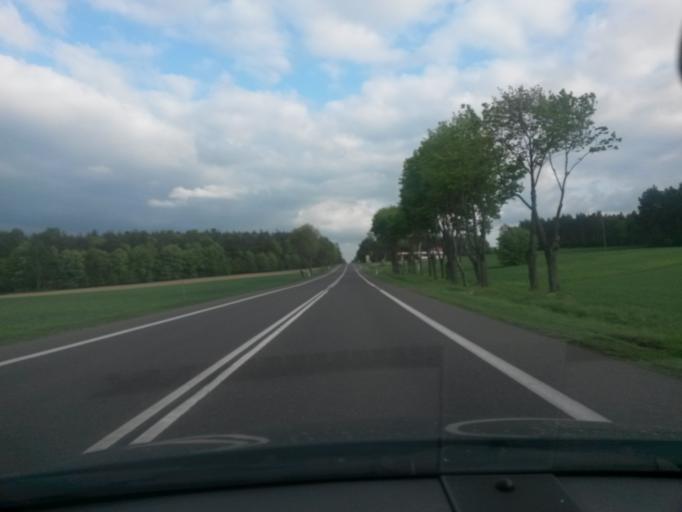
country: PL
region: Masovian Voivodeship
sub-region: Powiat plocki
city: Starozreby
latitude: 52.6681
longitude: 20.0716
